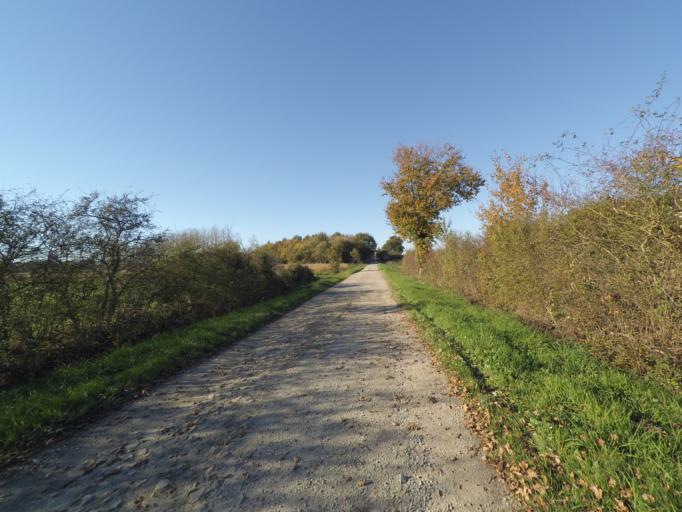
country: FR
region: Pays de la Loire
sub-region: Departement de la Loire-Atlantique
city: Remouille
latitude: 47.0179
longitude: -1.3910
